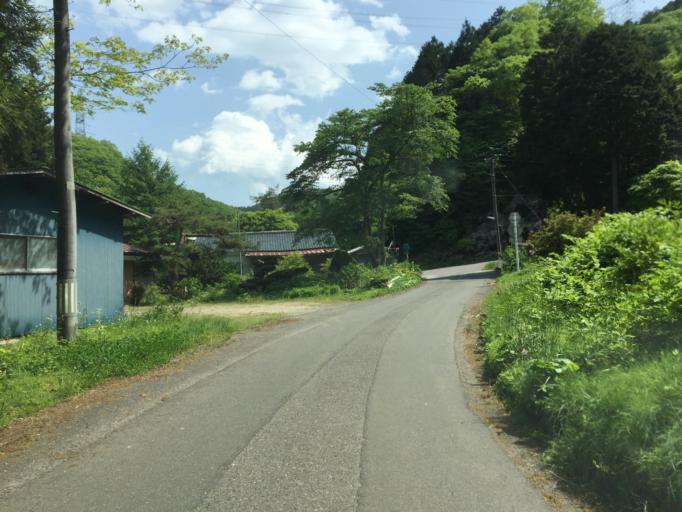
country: JP
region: Fukushima
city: Ishikawa
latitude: 37.0255
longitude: 140.5642
